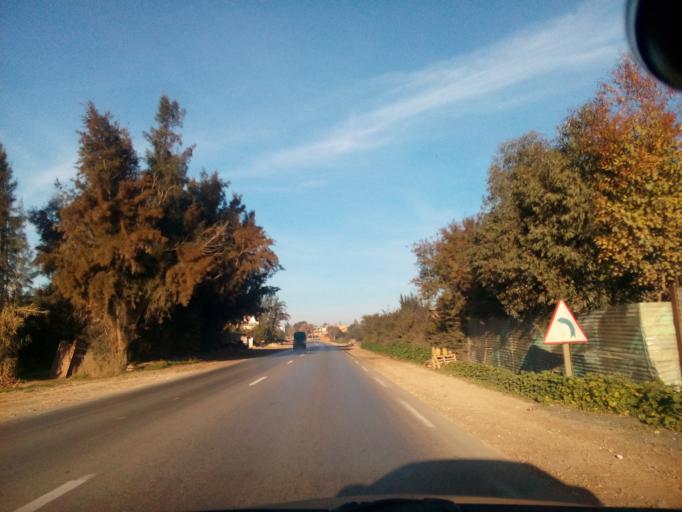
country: DZ
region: Relizane
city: Relizane
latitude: 35.7184
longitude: 0.3298
